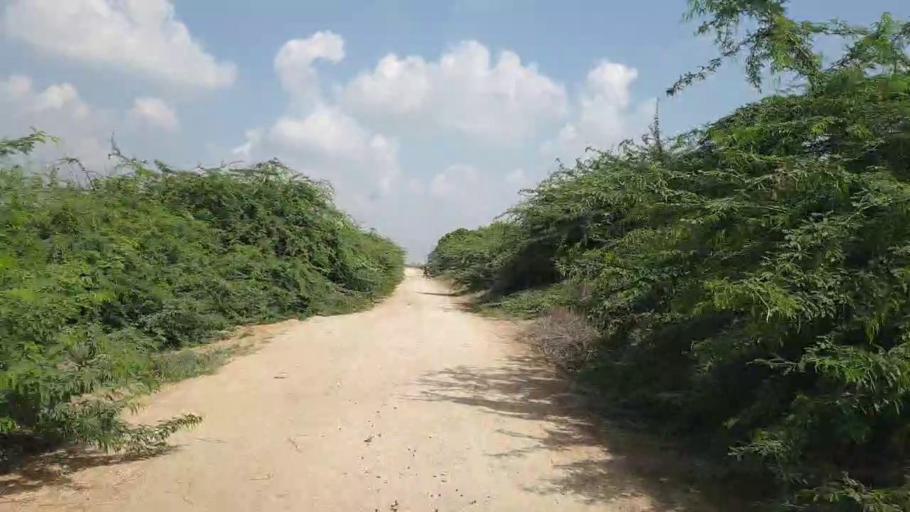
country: PK
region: Sindh
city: Badin
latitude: 24.4794
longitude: 68.6430
